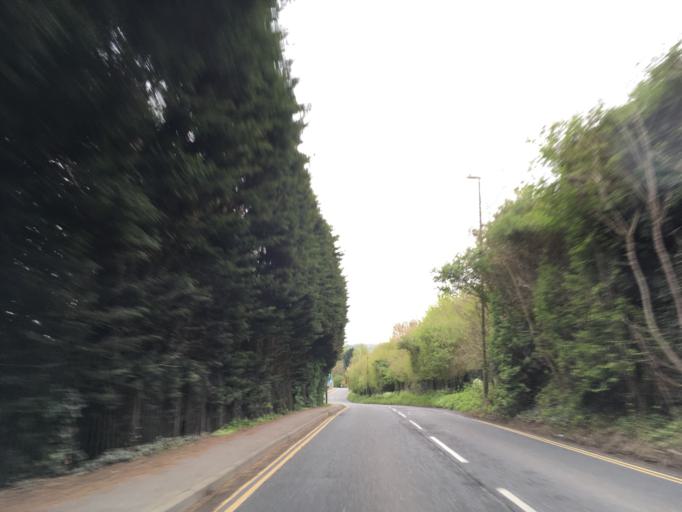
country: GB
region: England
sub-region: Gloucestershire
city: Stroud
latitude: 51.7359
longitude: -2.2336
